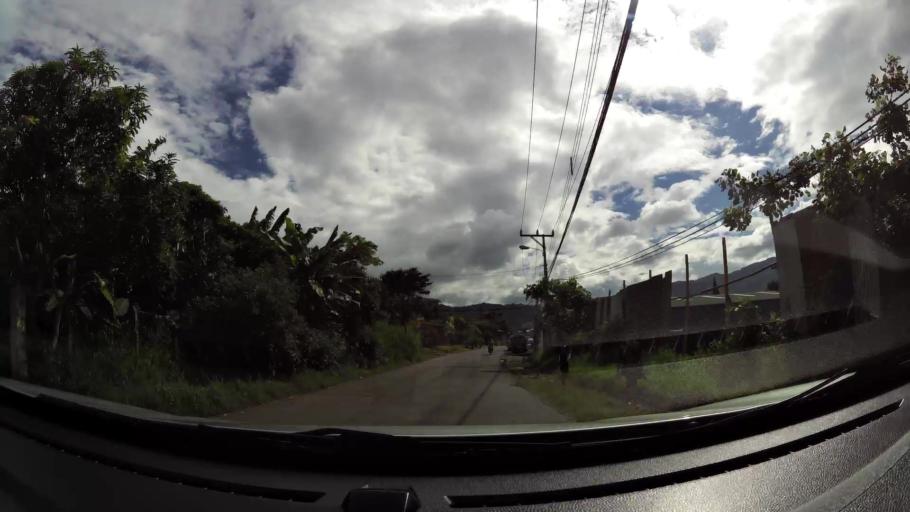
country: CR
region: San Jose
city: San Rafael Arriba
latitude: 9.8798
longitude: -84.0766
